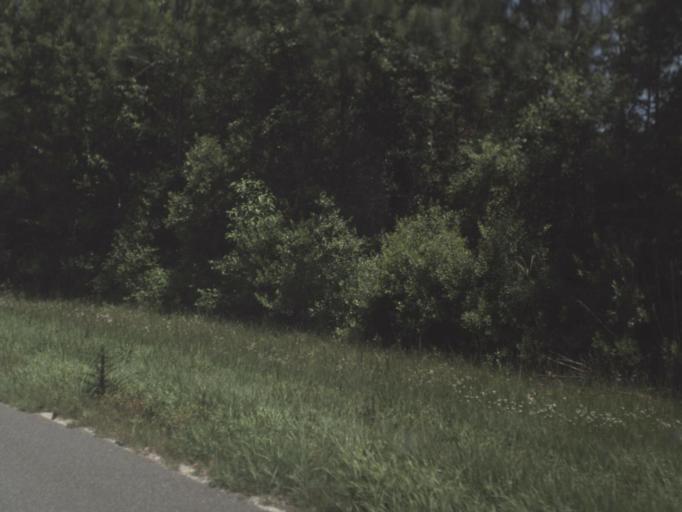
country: US
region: Florida
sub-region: Baker County
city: Macclenny
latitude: 30.2579
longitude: -82.2505
